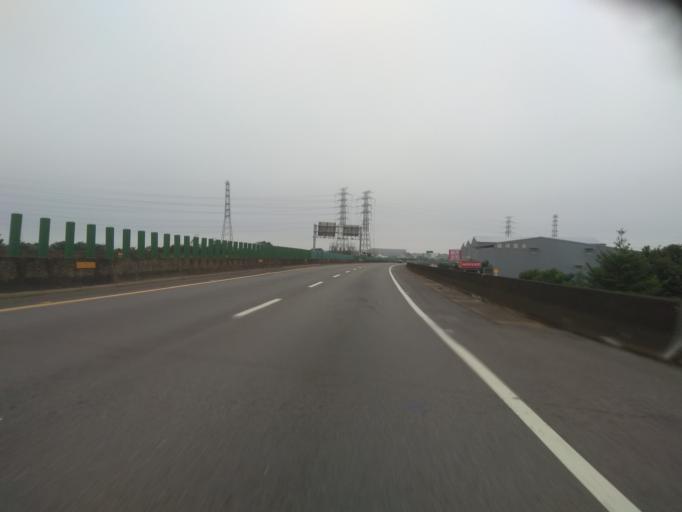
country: TW
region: Taiwan
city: Taoyuan City
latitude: 24.9842
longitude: 121.1287
